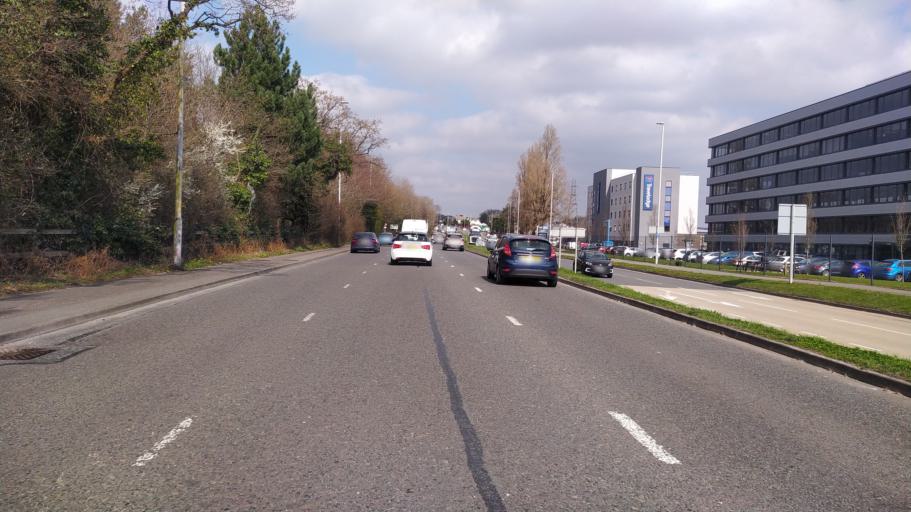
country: GB
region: England
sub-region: Dorset
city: Broadstone
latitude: 50.7409
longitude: -1.9872
